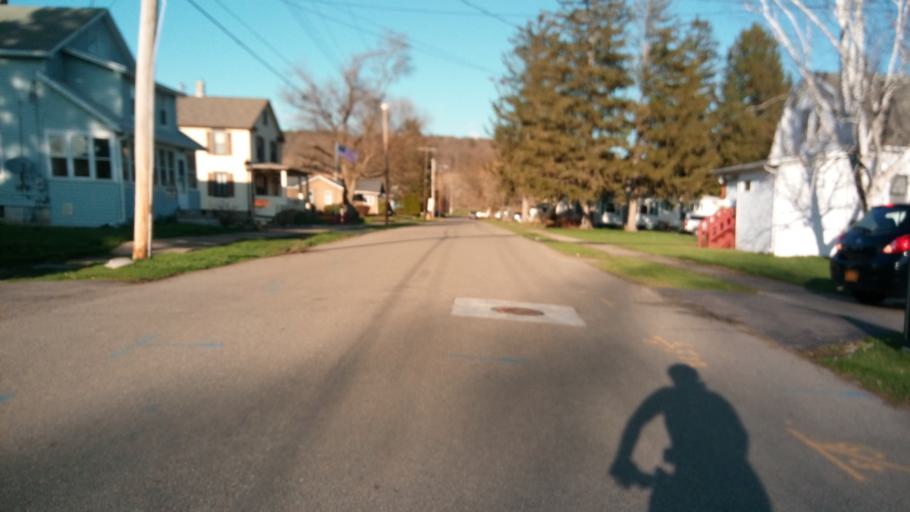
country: US
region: New York
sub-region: Chemung County
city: Elmira
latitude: 42.0779
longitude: -76.7820
